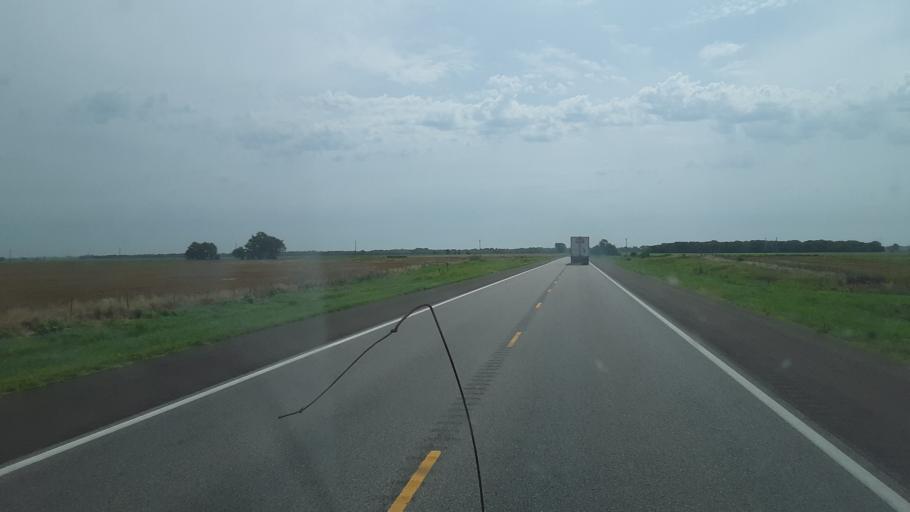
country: US
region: Kansas
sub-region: Reno County
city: Nickerson
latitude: 37.9850
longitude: -98.1655
